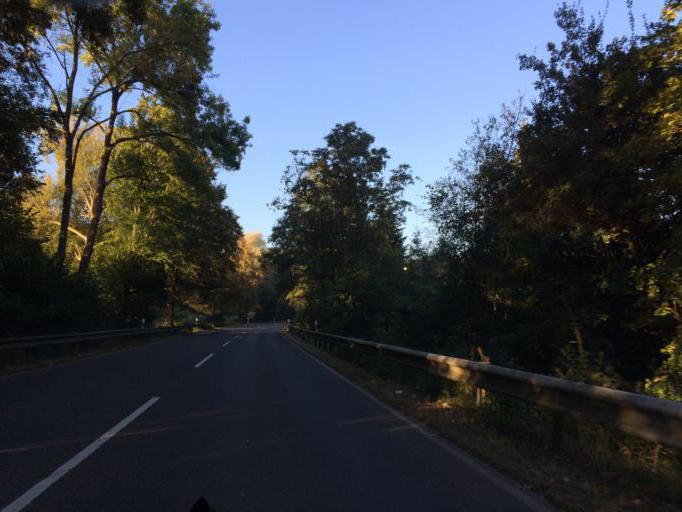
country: DE
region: North Rhine-Westphalia
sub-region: Regierungsbezirk Koln
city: Wachtberg
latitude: 50.6488
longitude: 7.1083
